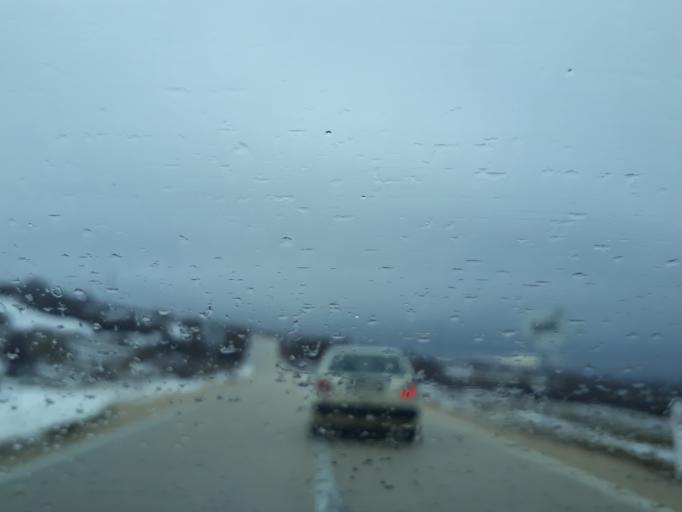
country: BA
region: Federation of Bosnia and Herzegovina
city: Tomislavgrad
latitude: 43.7916
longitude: 17.2195
